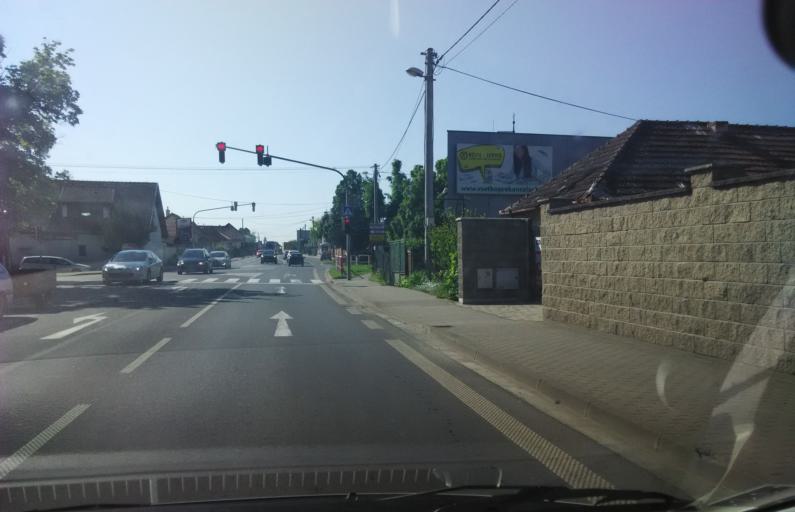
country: SK
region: Nitriansky
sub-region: Okres Nitra
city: Nitra
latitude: 48.2735
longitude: 18.0988
